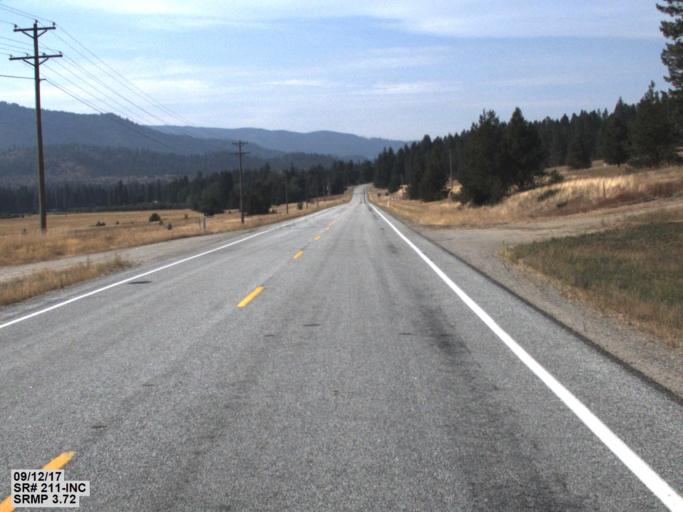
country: US
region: Washington
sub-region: Pend Oreille County
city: Newport
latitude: 48.1456
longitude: -117.2947
